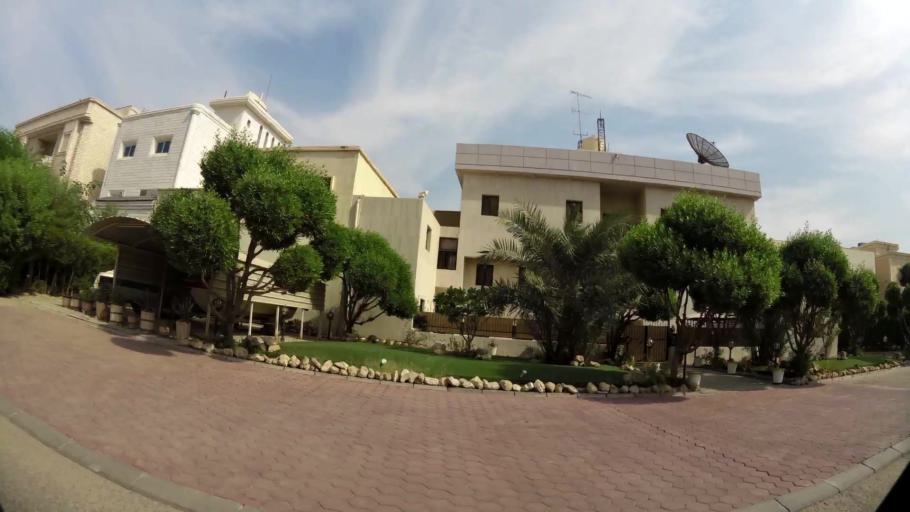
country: KW
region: Al Asimah
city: Ash Shamiyah
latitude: 29.3417
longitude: 47.9760
